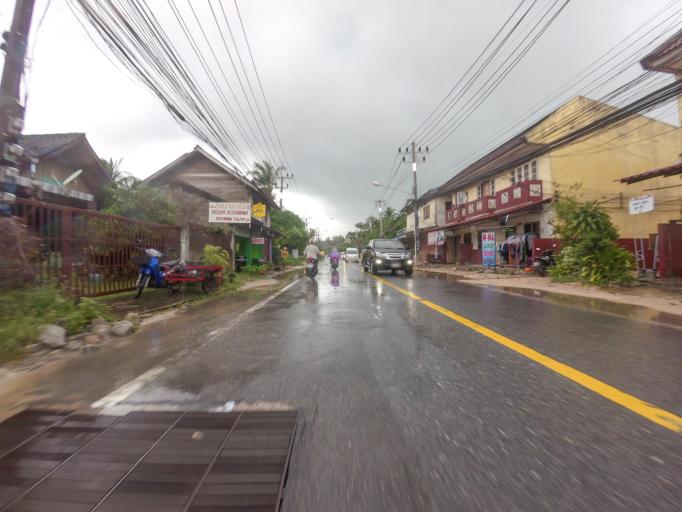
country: TH
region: Surat Thani
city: Ko Samui
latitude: 9.4454
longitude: 100.0252
